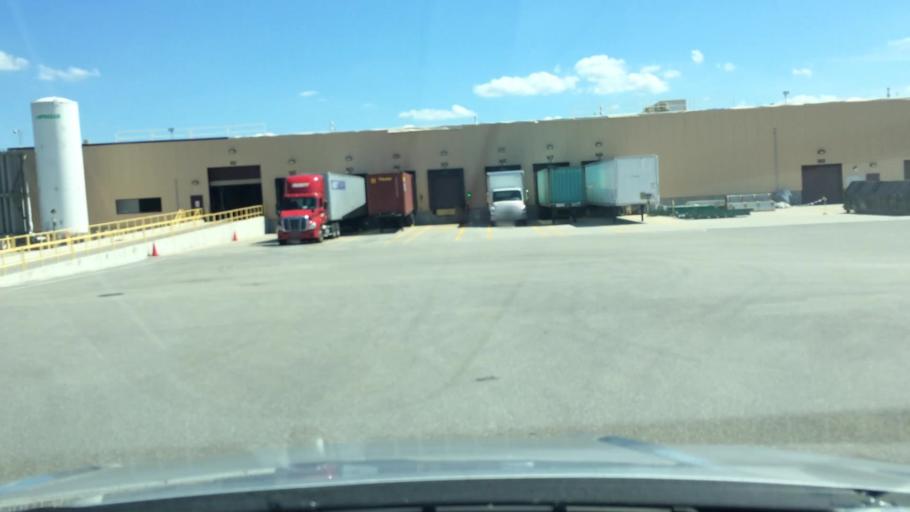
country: US
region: Tennessee
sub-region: McMinn County
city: Athens
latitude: 35.4788
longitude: -84.6434
